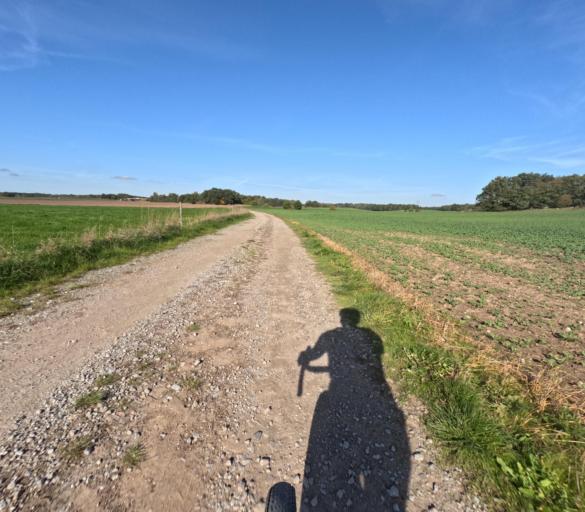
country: DE
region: Saxony
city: Radeburg
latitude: 51.1694
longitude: 13.7578
